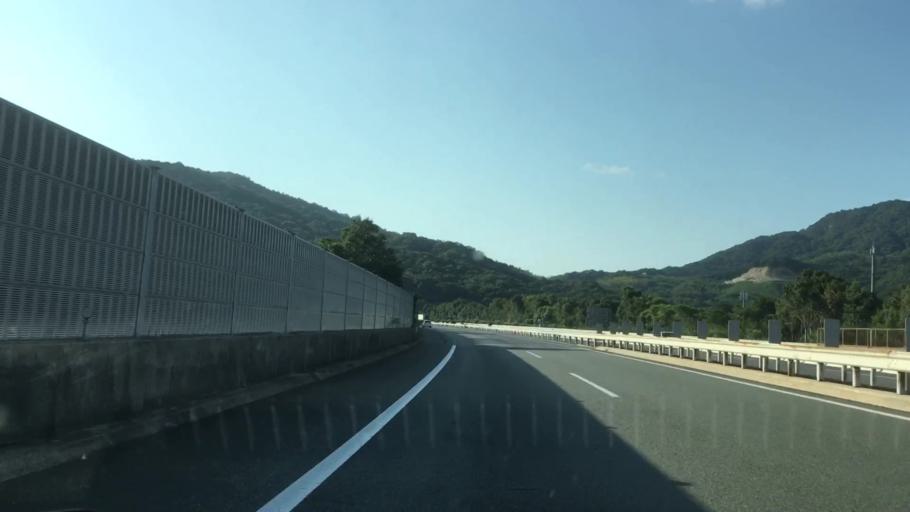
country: JP
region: Yamaguchi
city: Hofu
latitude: 34.0681
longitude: 131.6013
